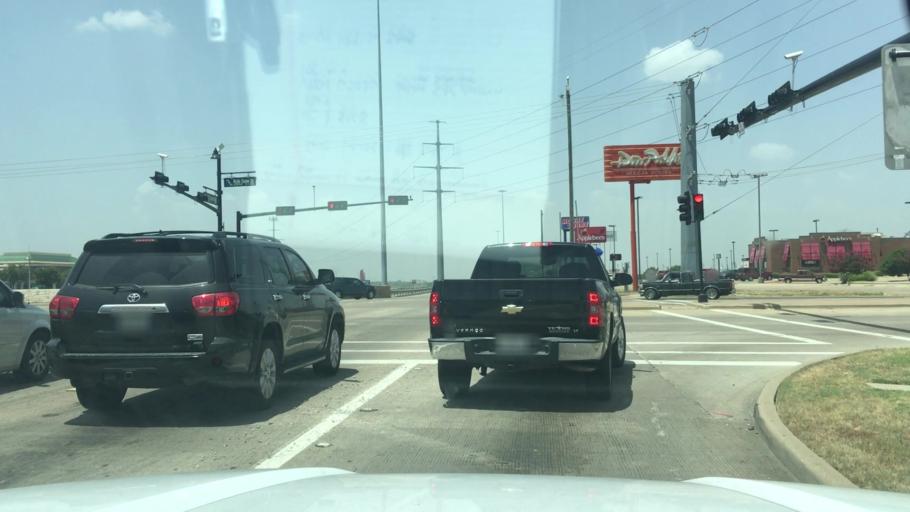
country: US
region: Texas
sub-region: Tarrant County
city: North Richland Hills
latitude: 32.8408
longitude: -97.2384
